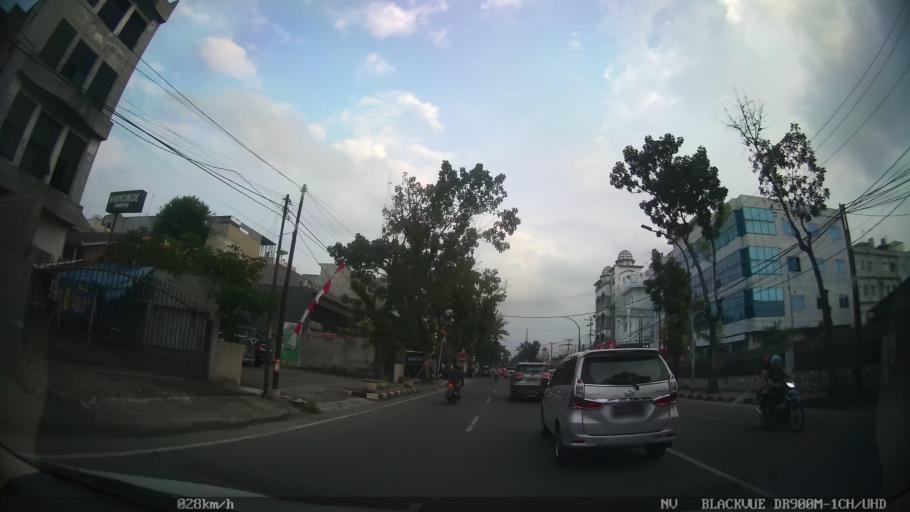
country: ID
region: North Sumatra
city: Medan
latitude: 3.6052
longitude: 98.6692
